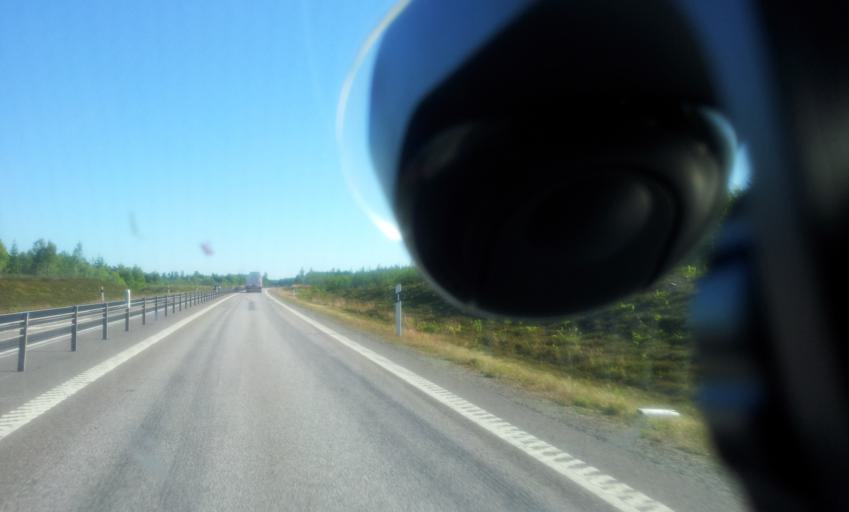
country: SE
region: Kalmar
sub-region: Torsas Kommun
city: Torsas
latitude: 56.4804
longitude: 16.0816
